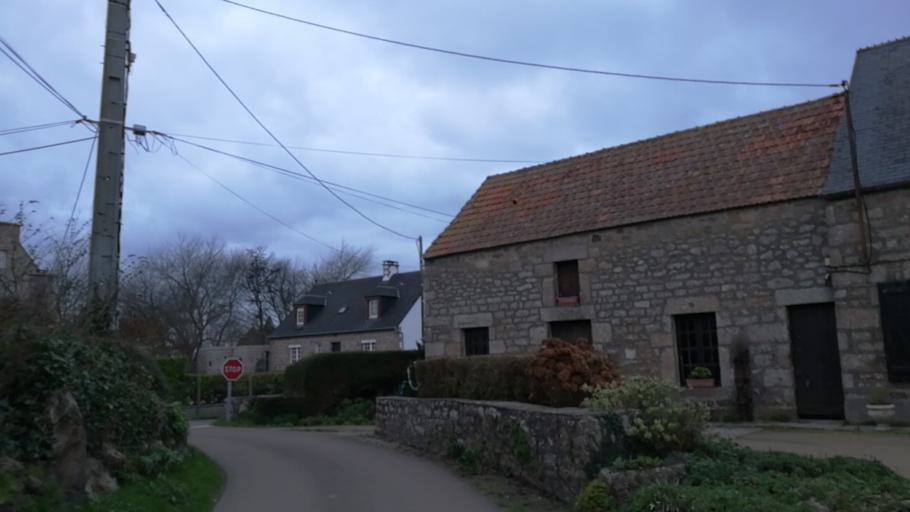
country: FR
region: Lower Normandy
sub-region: Departement de la Manche
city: Fermanville
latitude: 49.6905
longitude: -1.4632
